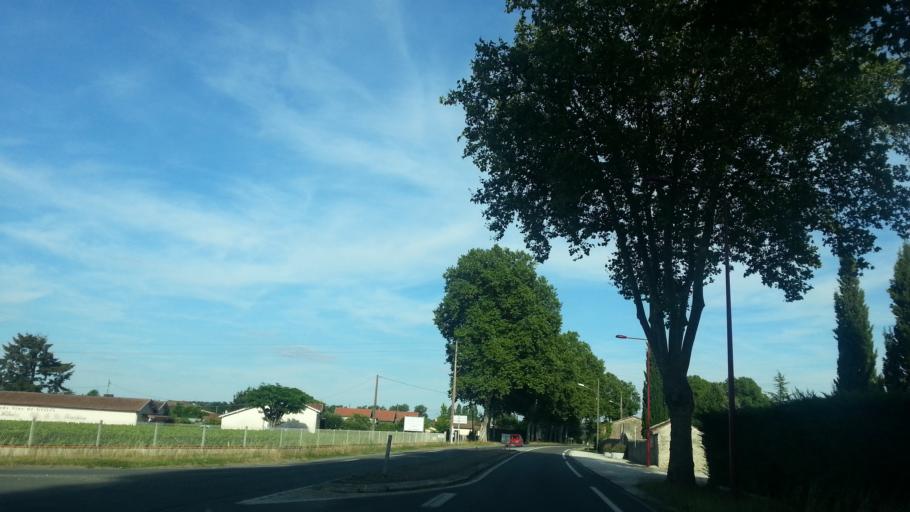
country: FR
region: Aquitaine
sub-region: Departement de la Gironde
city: Castres-Gironde
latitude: 44.6959
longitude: -0.4405
